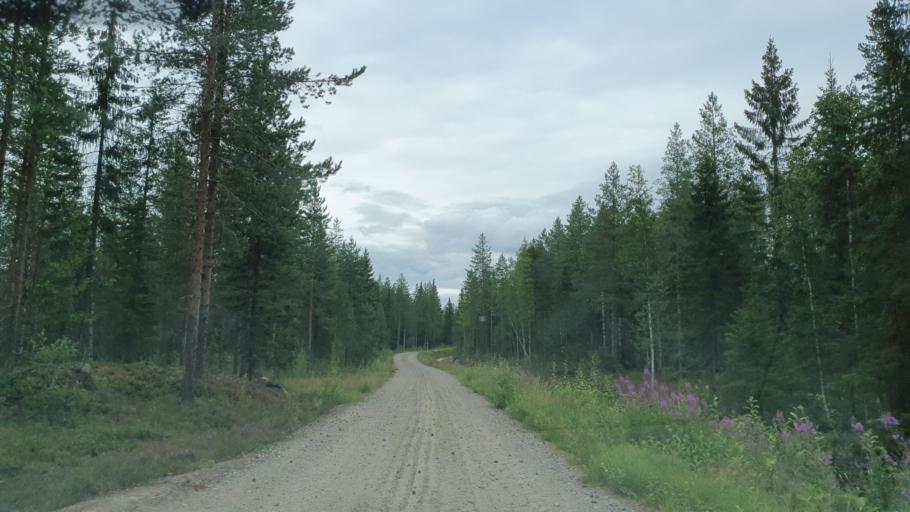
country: FI
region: Kainuu
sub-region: Kehys-Kainuu
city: Kuhmo
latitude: 64.2033
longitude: 29.3940
